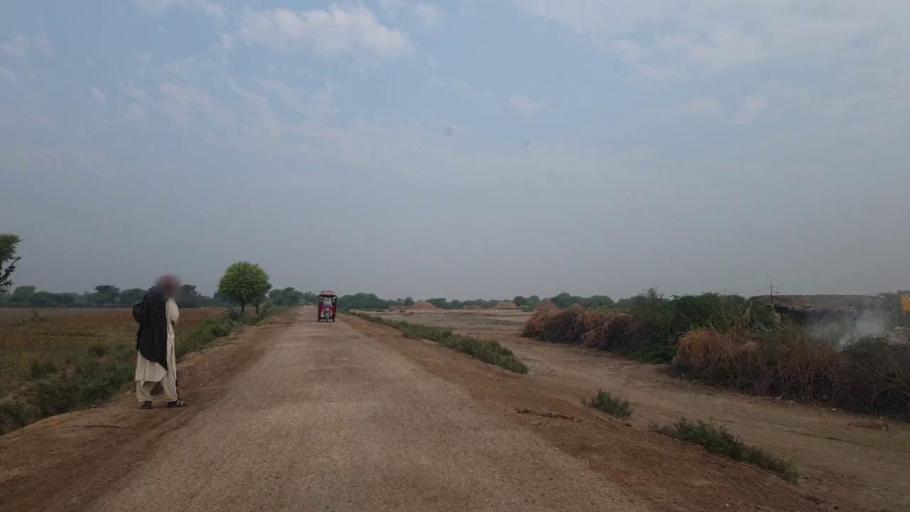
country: PK
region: Sindh
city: Tando Bago
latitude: 24.8035
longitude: 68.8731
